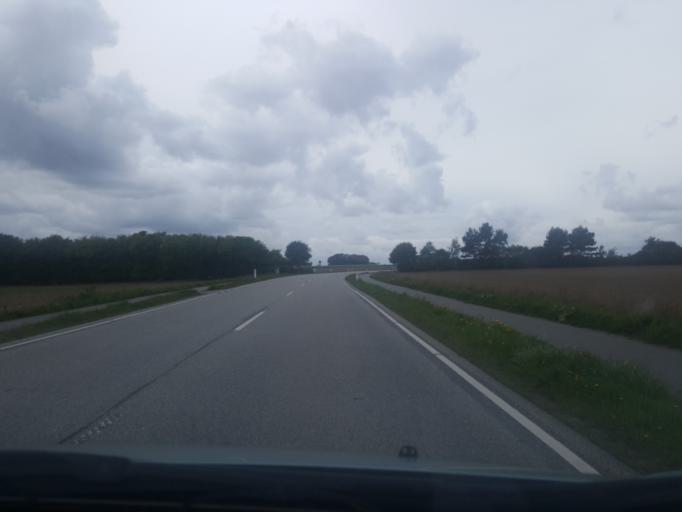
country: DK
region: Zealand
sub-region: Guldborgsund Kommune
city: Nykobing Falster
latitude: 54.7018
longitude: 11.9348
